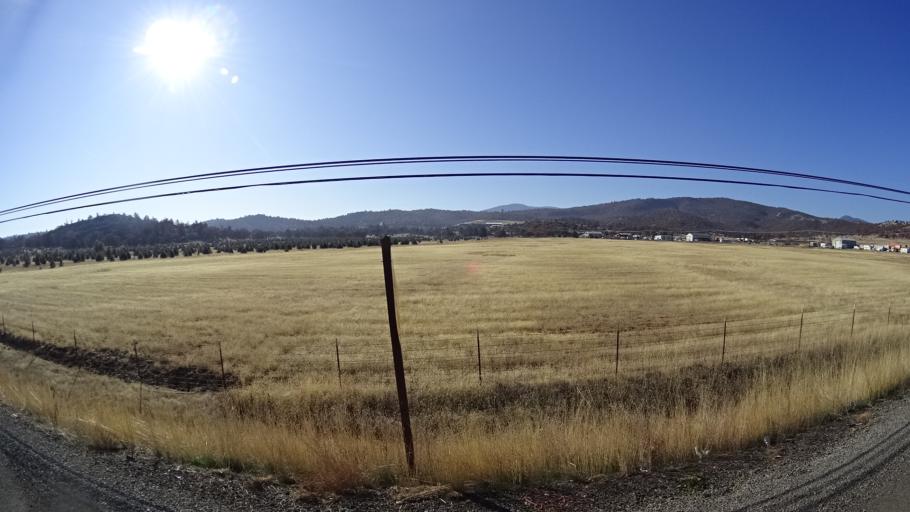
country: US
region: California
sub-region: Siskiyou County
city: Yreka
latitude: 41.7112
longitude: -122.5961
